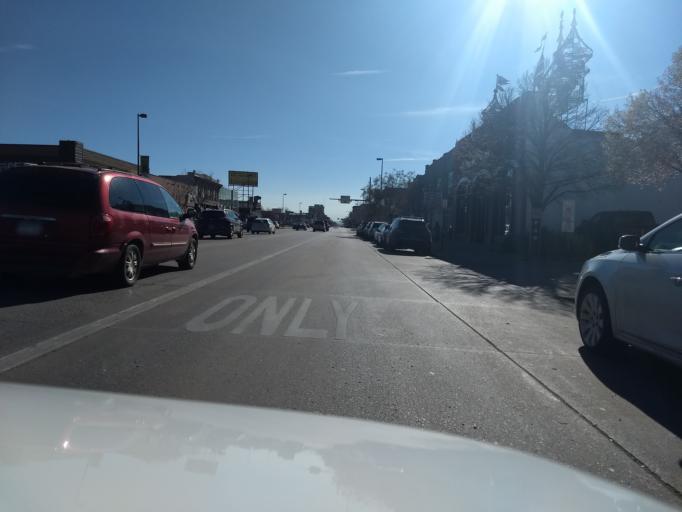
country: US
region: Colorado
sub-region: Denver County
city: Denver
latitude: 39.7239
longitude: -104.9876
